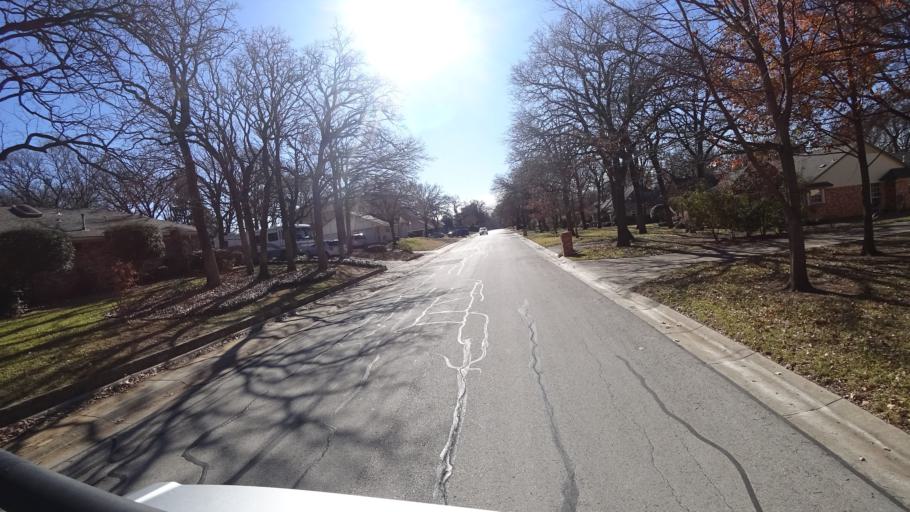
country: US
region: Texas
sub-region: Denton County
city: Lewisville
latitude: 33.0235
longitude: -97.0144
